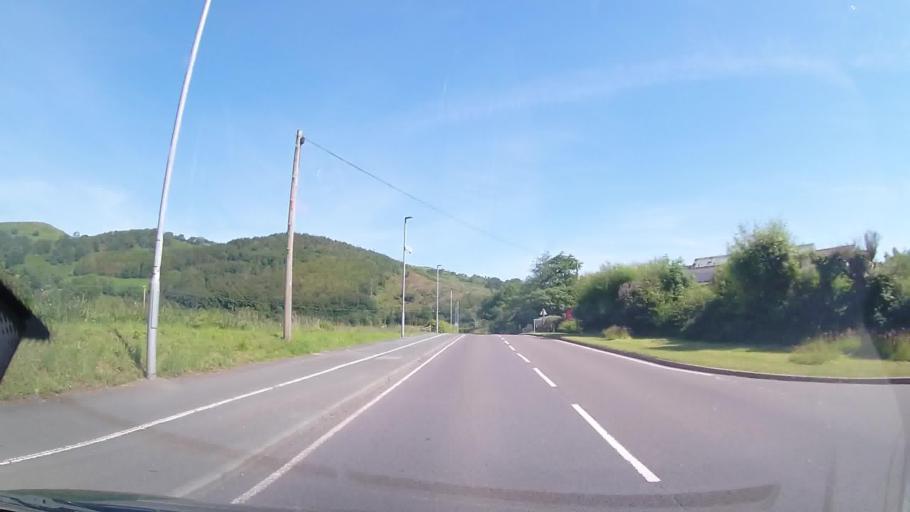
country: GB
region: Wales
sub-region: Sir Powys
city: Machynlleth
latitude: 52.5952
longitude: -3.8555
